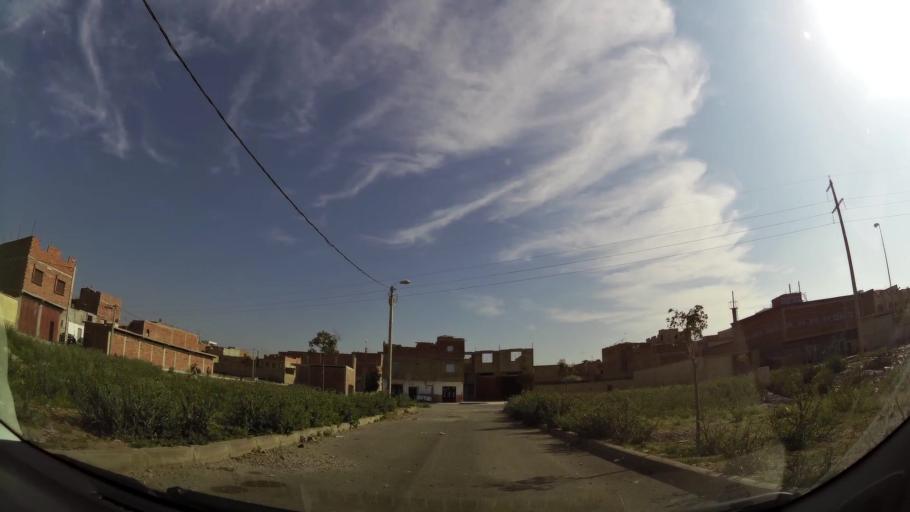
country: MA
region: Oriental
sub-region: Oujda-Angad
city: Oujda
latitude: 34.7218
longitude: -1.8837
